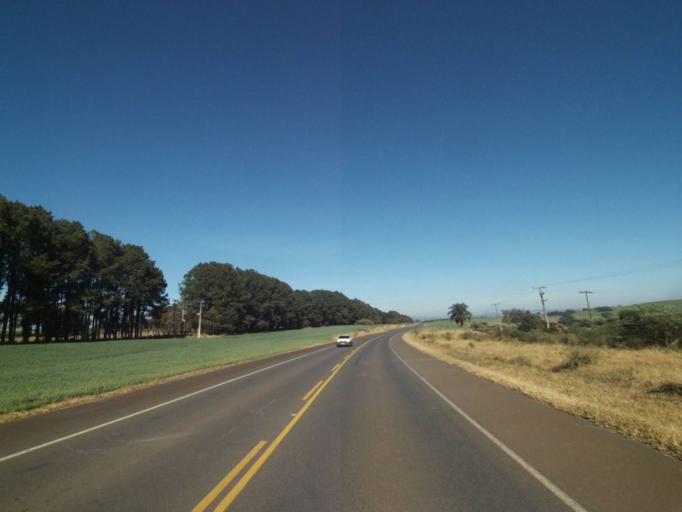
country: BR
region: Parana
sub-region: Tibagi
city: Tibagi
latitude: -24.4148
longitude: -50.3661
